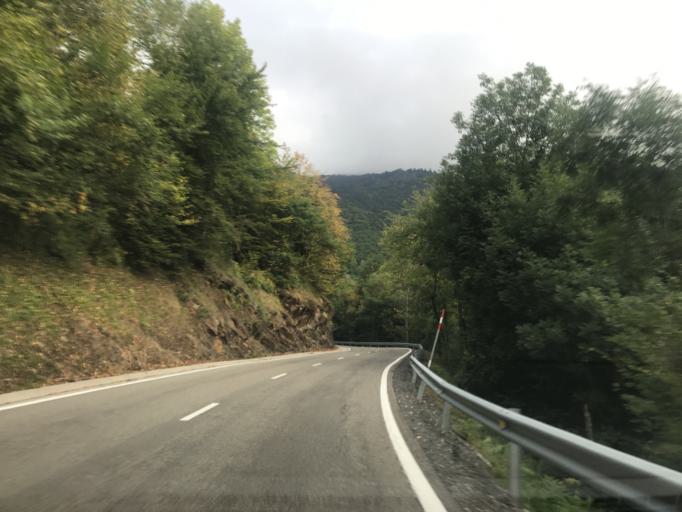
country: ES
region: Catalonia
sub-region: Provincia de Lleida
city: Les
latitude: 42.7803
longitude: 0.6799
